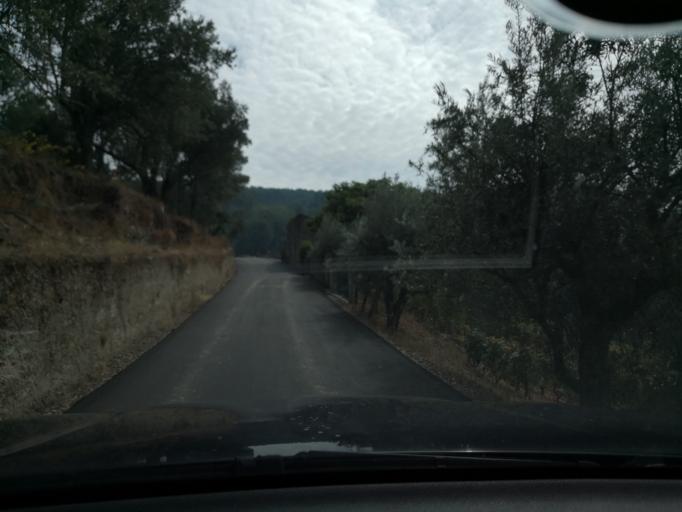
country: PT
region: Vila Real
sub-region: Sabrosa
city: Vilela
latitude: 41.2161
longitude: -7.6852
